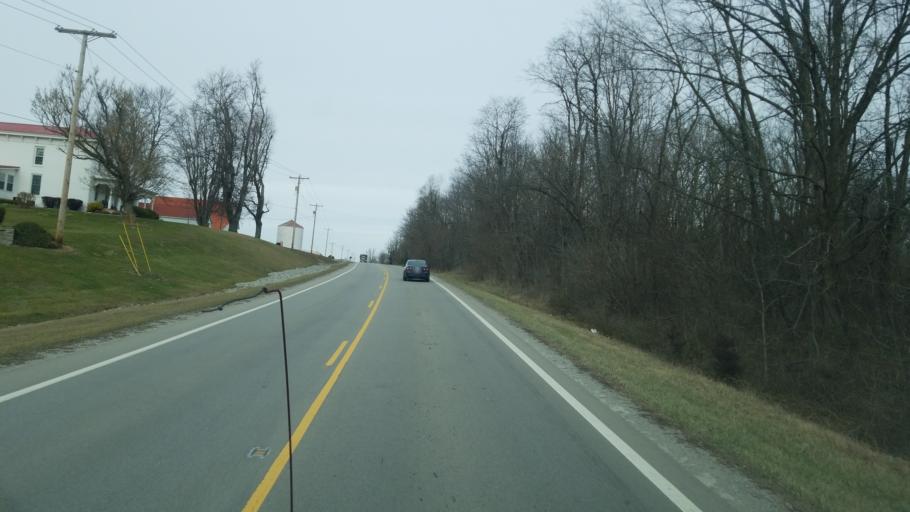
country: US
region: Ohio
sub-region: Adams County
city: Winchester
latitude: 39.0034
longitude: -83.7096
